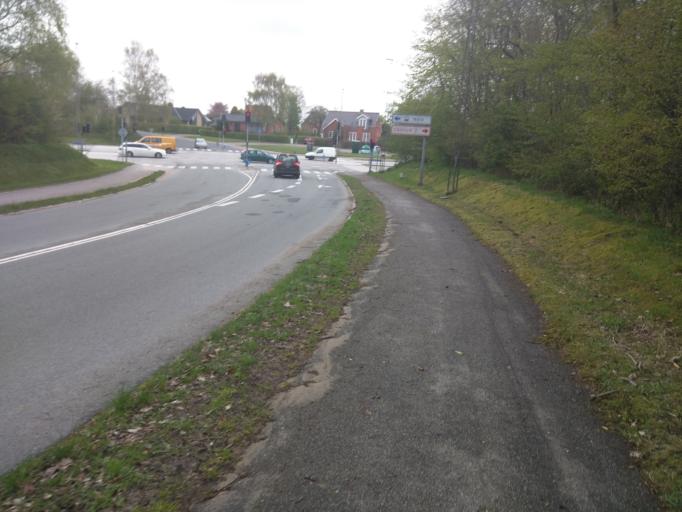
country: DK
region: Central Jutland
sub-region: Viborg Kommune
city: Viborg
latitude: 56.4671
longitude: 9.4143
